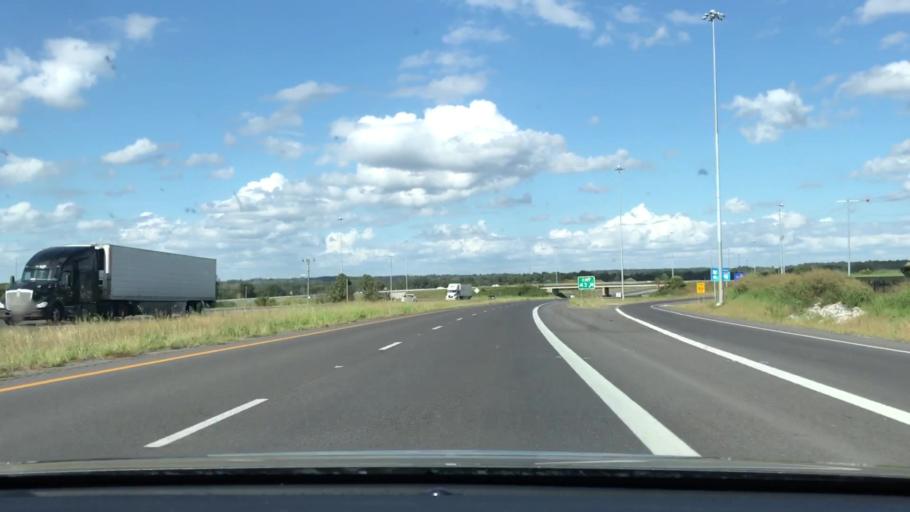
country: US
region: Kentucky
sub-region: Marshall County
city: Benton
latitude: 36.8647
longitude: -88.3666
